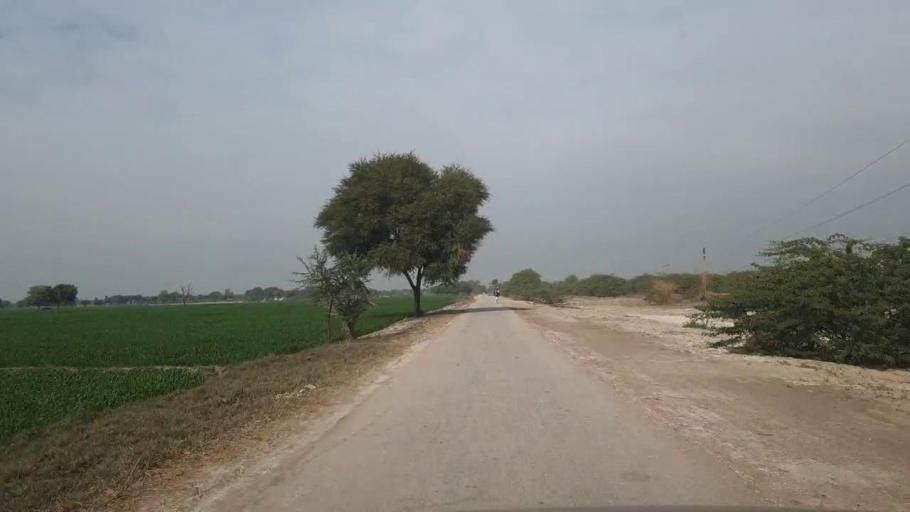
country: PK
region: Sindh
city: Nawabshah
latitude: 26.1095
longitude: 68.4813
